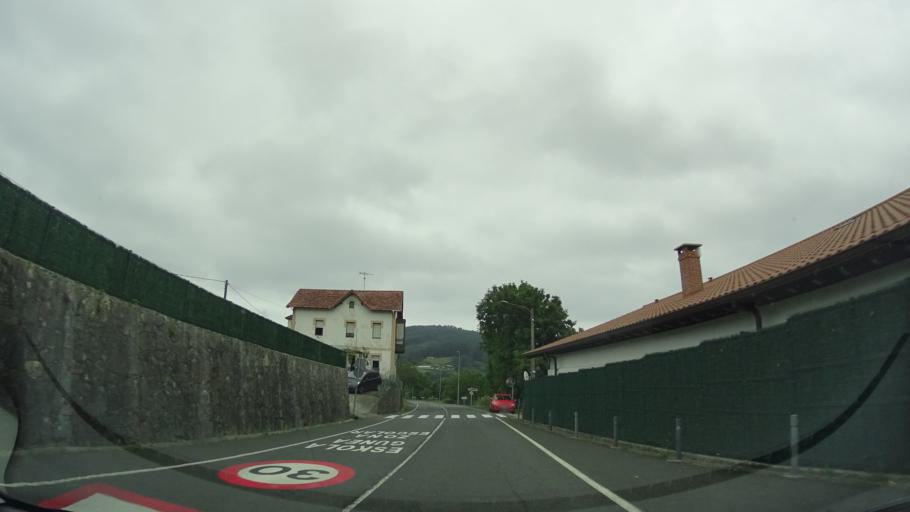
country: ES
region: Basque Country
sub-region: Bizkaia
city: Elexalde
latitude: 43.4140
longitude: -2.9026
